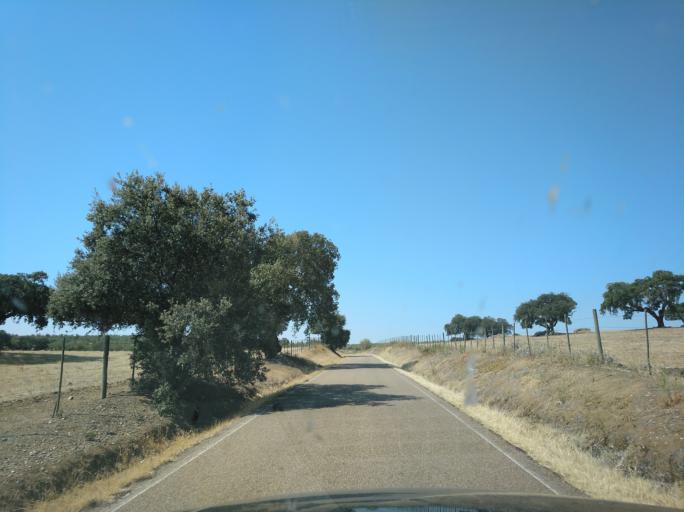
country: PT
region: Portalegre
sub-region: Campo Maior
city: Campo Maior
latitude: 39.0443
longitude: -7.0249
